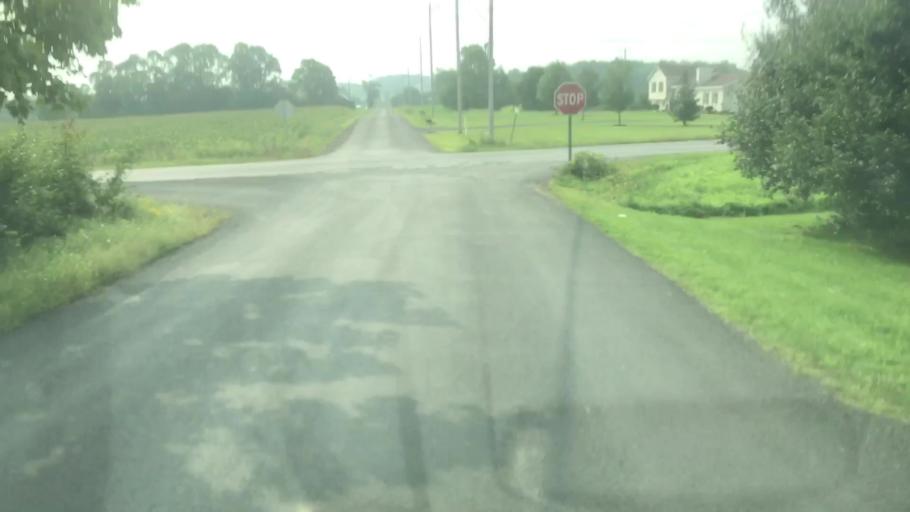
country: US
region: New York
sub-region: Onondaga County
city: Skaneateles
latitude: 42.9063
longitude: -76.4507
